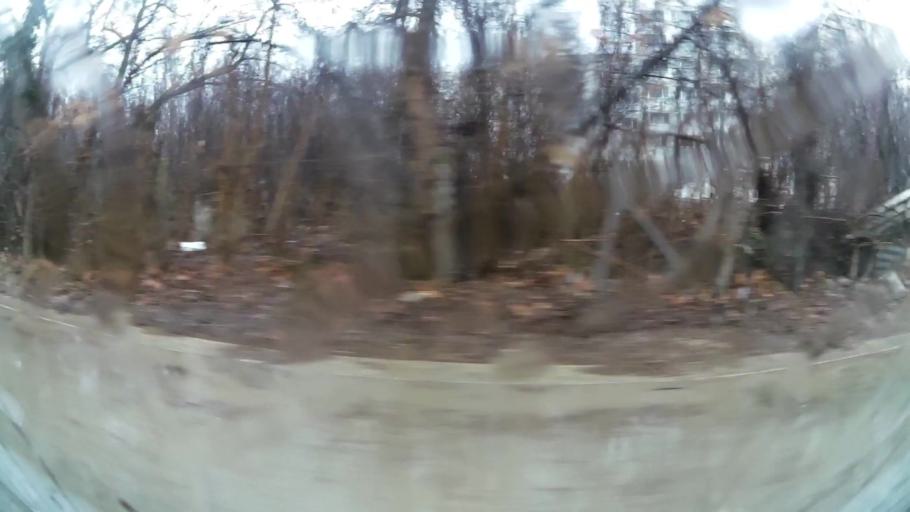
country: BG
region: Sofia-Capital
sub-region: Stolichna Obshtina
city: Sofia
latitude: 42.6293
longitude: 23.3657
